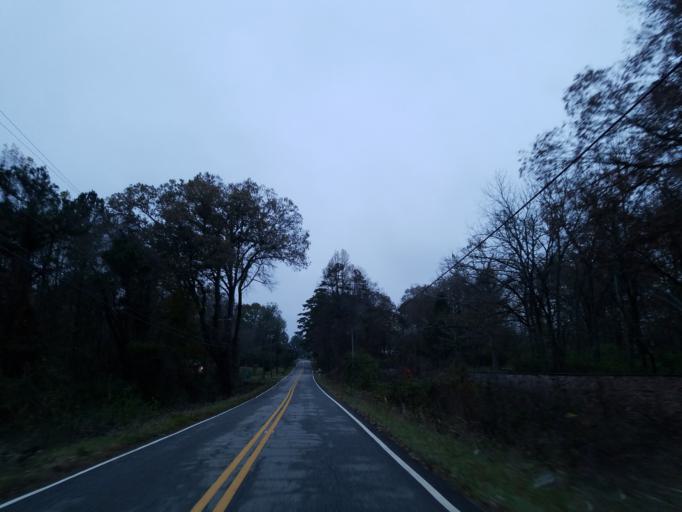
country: US
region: Georgia
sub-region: Cherokee County
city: Ball Ground
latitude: 34.3507
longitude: -84.3758
